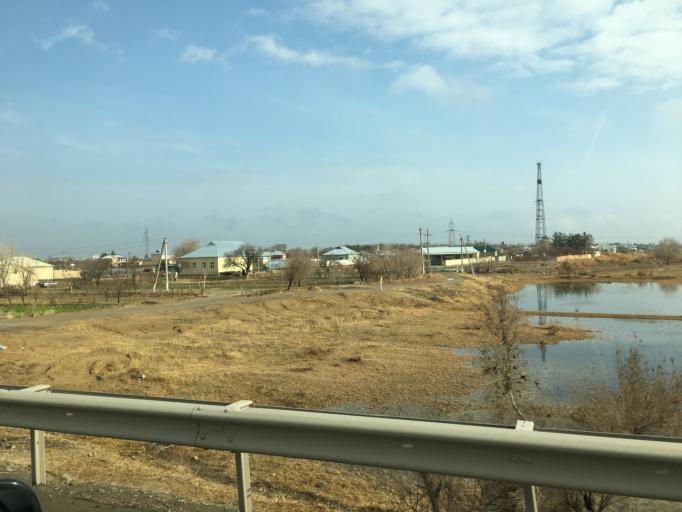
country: TM
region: Mary
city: Mary
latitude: 37.5513
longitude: 61.8631
